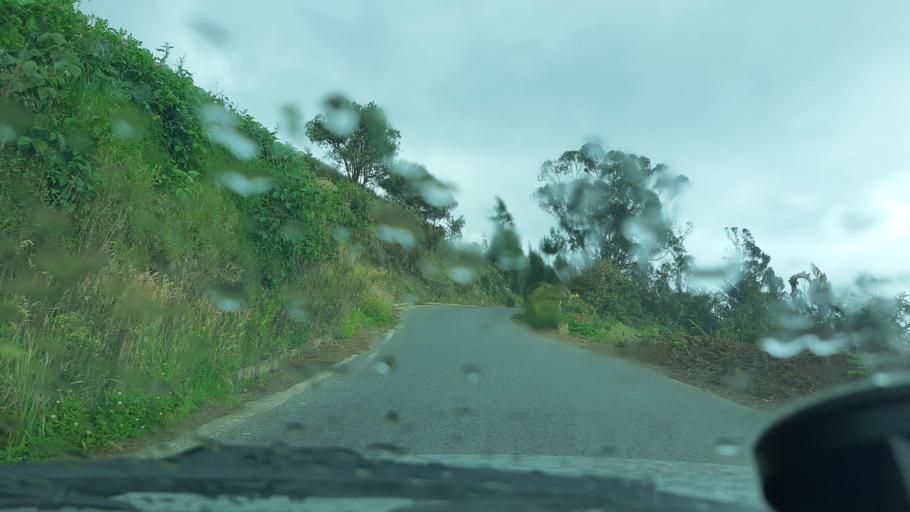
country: CO
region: Cundinamarca
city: Umbita
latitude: 5.2199
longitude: -73.4733
